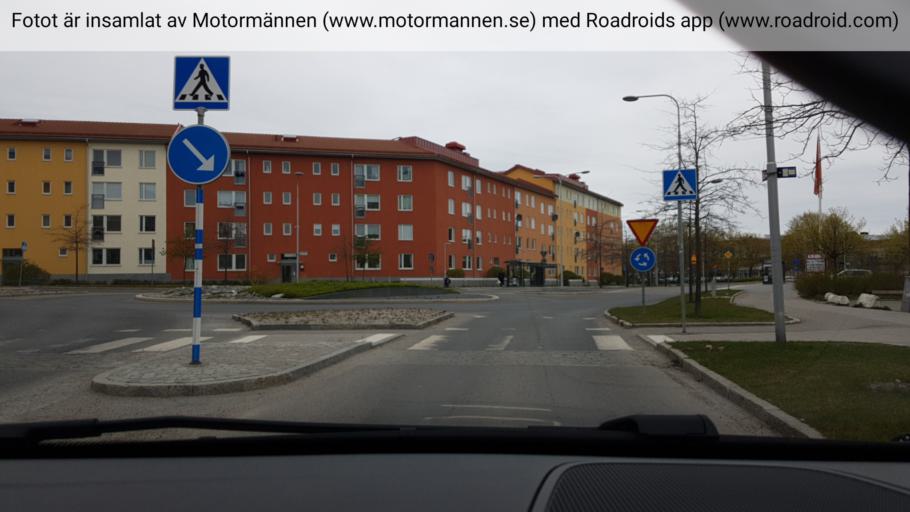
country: SE
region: Stockholm
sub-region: Huddinge Kommun
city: Huddinge
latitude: 59.2404
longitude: 17.9944
